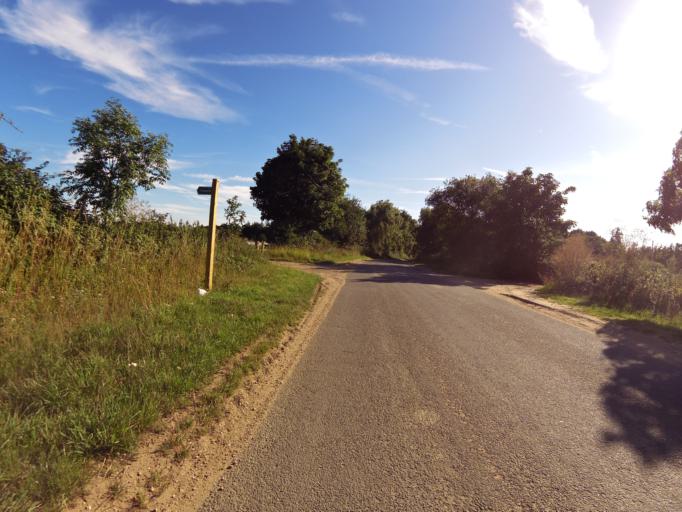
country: GB
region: England
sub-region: Suffolk
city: Kesgrave
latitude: 52.0272
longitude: 1.2575
